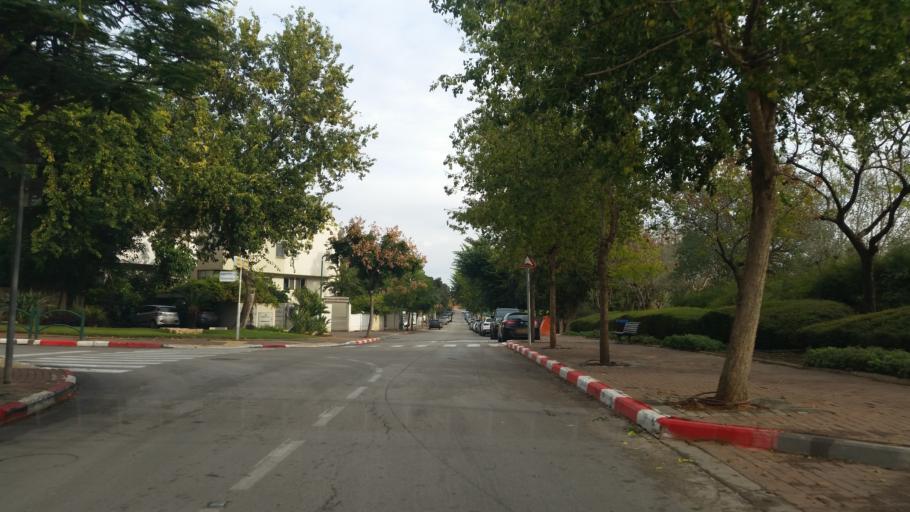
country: IL
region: Tel Aviv
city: Ramat HaSharon
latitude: 32.1508
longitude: 34.8499
